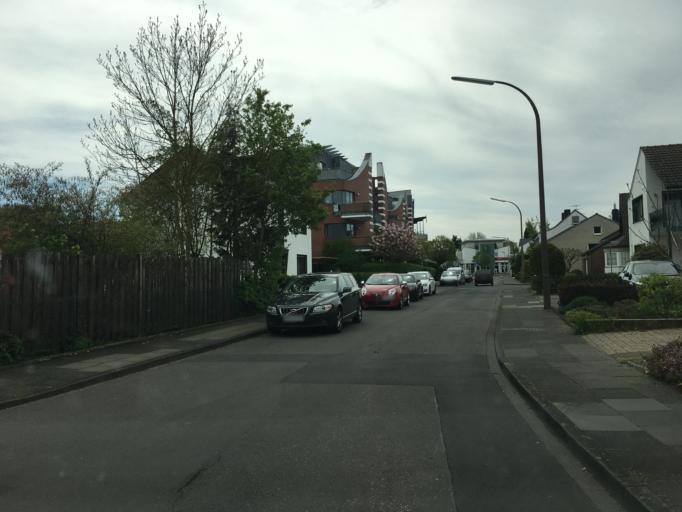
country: DE
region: North Rhine-Westphalia
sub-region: Regierungsbezirk Koln
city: Erftstadt
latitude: 50.8013
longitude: 6.7750
